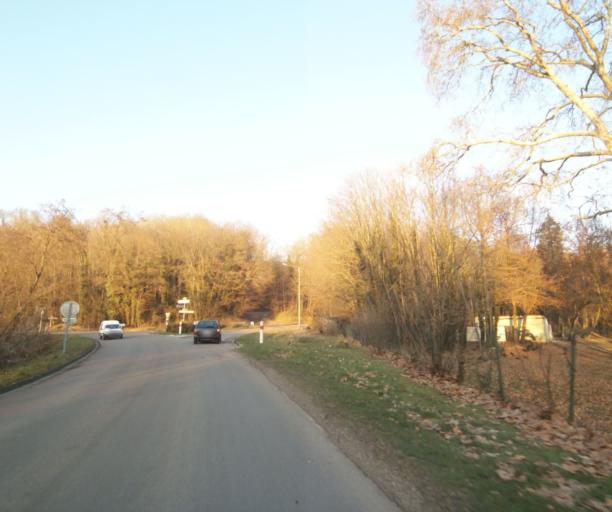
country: FR
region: Champagne-Ardenne
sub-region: Departement de la Haute-Marne
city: Bienville
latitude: 48.6107
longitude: 5.0467
